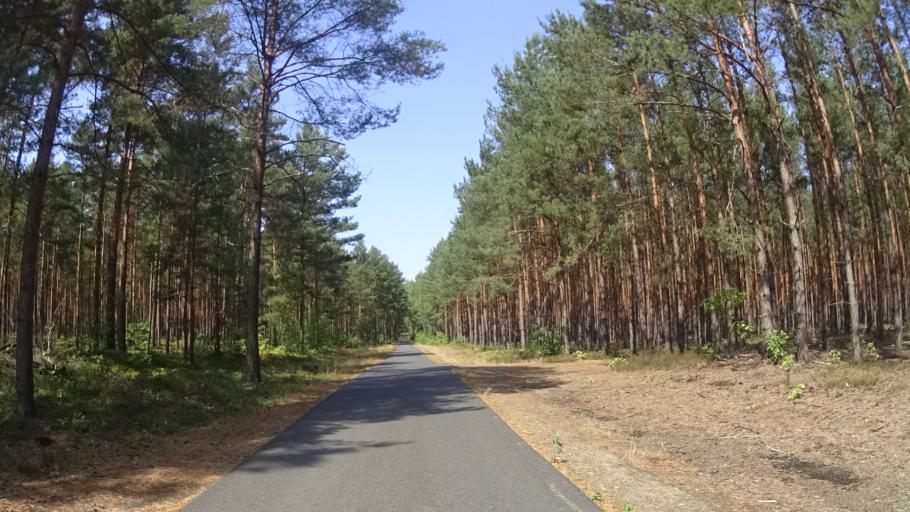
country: DE
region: Brandenburg
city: Tschernitz
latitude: 51.5954
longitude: 14.5955
